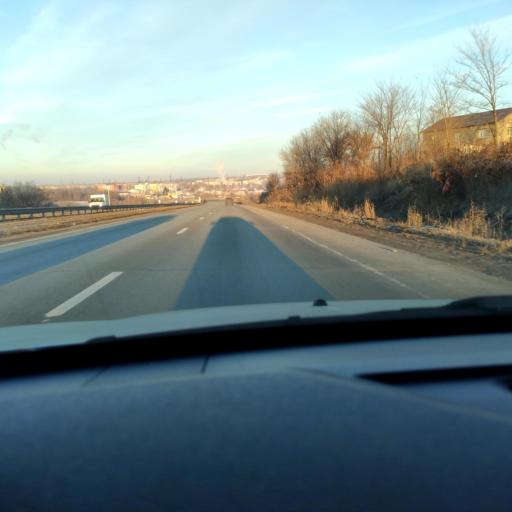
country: RU
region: Samara
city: Smyshlyayevka
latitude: 53.2639
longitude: 50.4104
